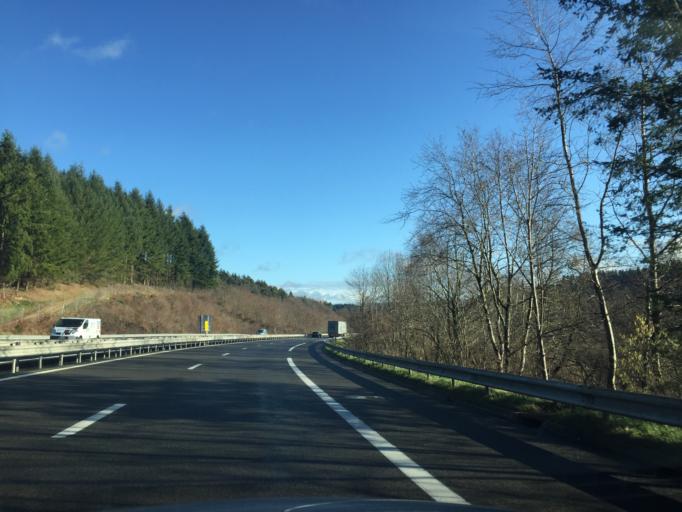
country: FR
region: Auvergne
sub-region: Departement du Puy-de-Dome
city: Saint-Remy-sur-Durolle
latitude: 45.8830
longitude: 3.6050
